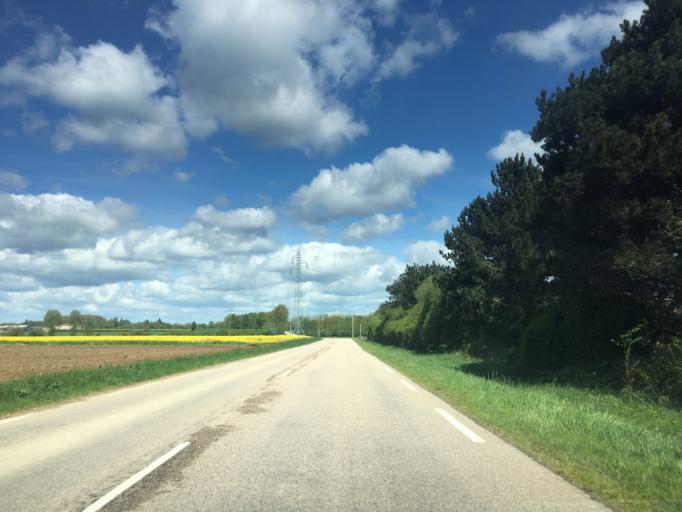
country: FR
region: Lower Normandy
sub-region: Departement de l'Orne
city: Rai
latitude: 48.8113
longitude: 0.5788
